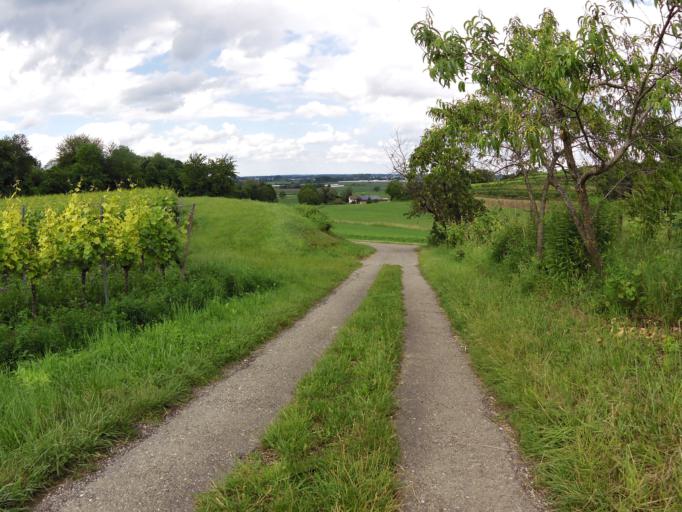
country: DE
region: Baden-Wuerttemberg
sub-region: Freiburg Region
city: Lahr
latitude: 48.3551
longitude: 7.8586
